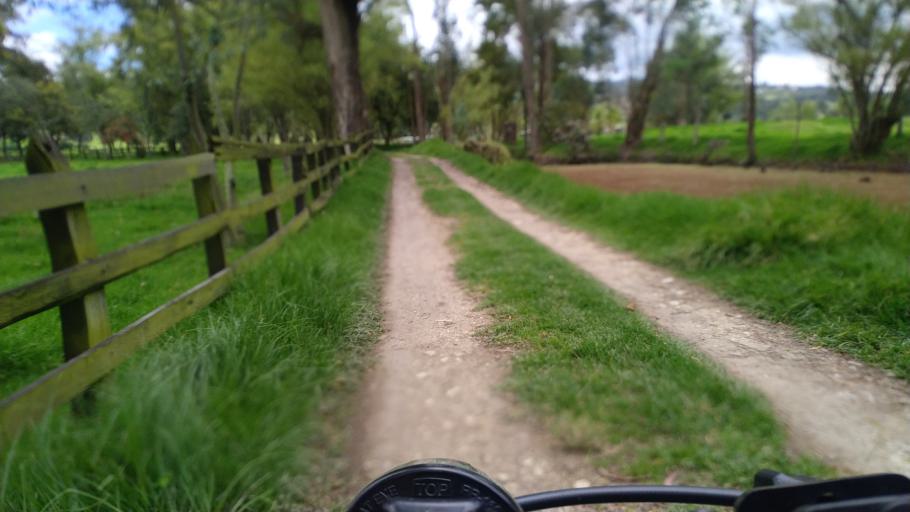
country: CO
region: Boyaca
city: Paipa
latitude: 5.7712
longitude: -73.0884
